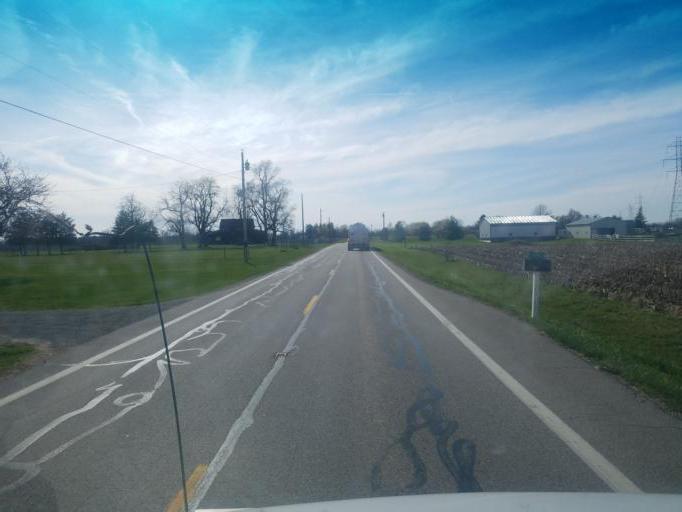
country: US
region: Ohio
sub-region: Union County
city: Richwood
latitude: 40.3468
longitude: -83.3204
